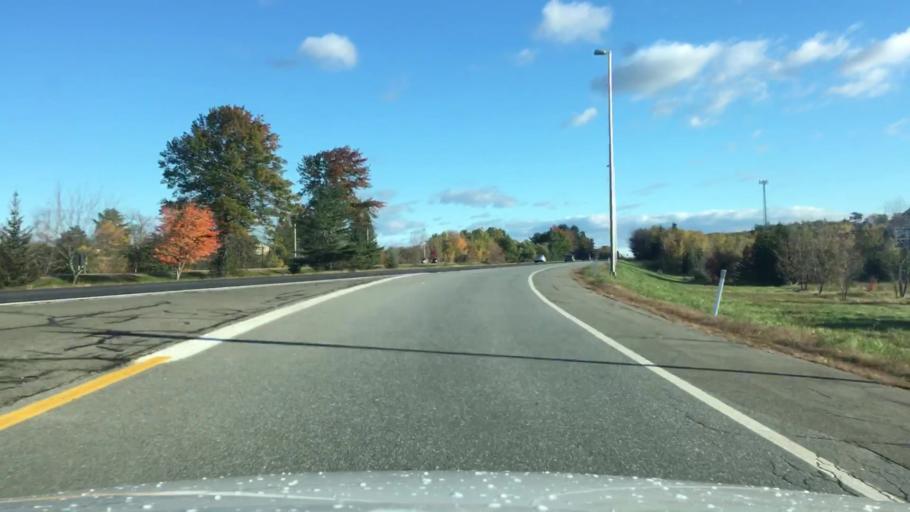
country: US
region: Maine
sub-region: Penobscot County
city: Veazie
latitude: 44.8334
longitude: -68.7402
